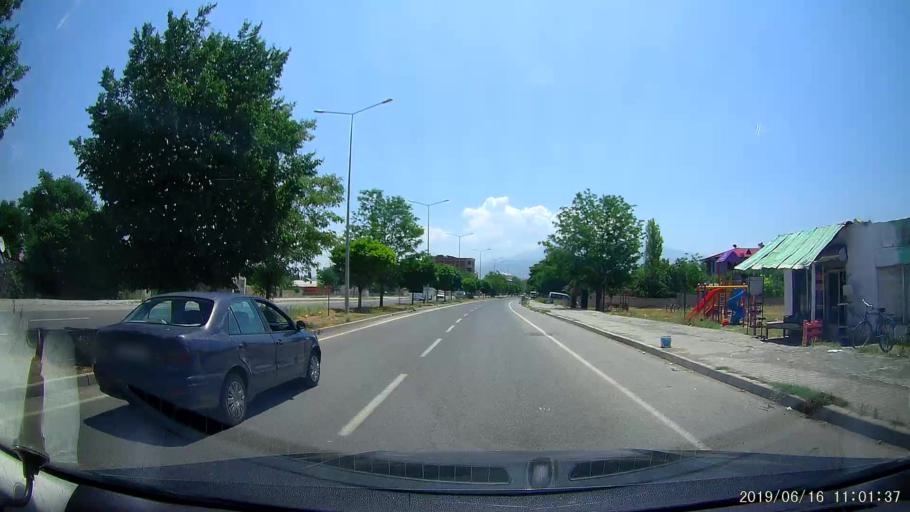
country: TR
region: Igdir
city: Igdir
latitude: 39.9138
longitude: 44.0516
